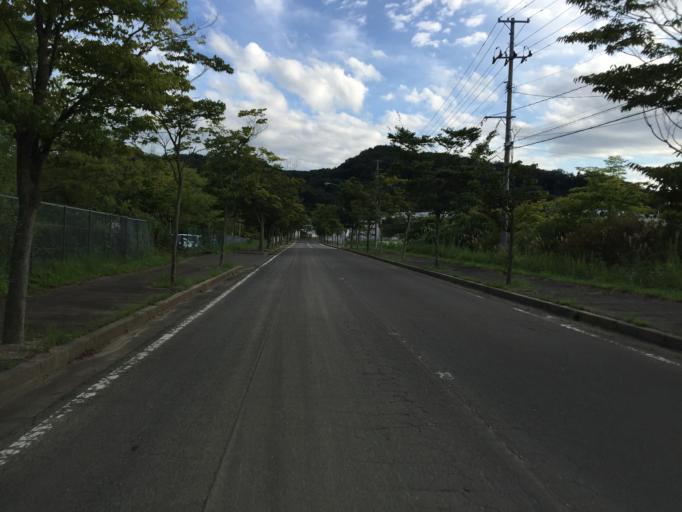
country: JP
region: Fukushima
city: Hobaramachi
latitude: 37.7892
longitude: 140.5198
